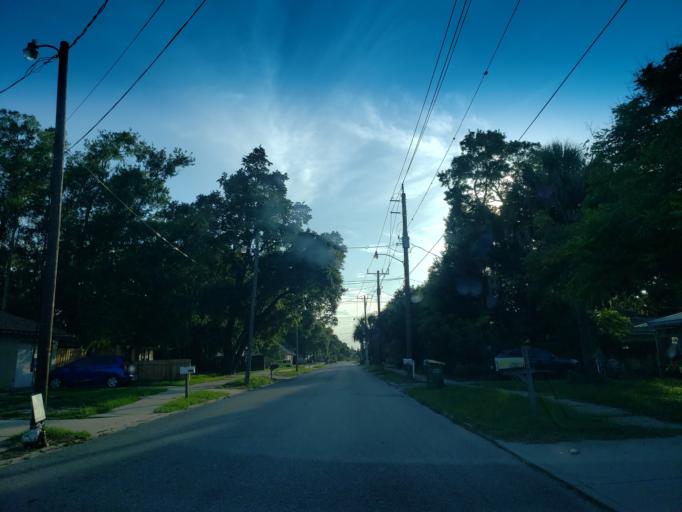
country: US
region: Florida
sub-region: Sarasota County
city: Sarasota
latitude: 27.3445
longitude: -82.5355
